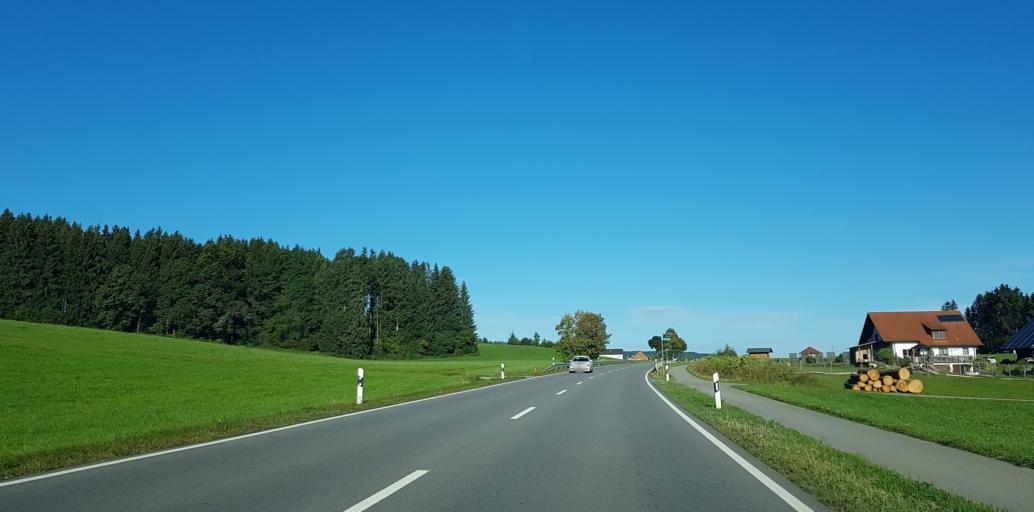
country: DE
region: Baden-Wuerttemberg
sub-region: Tuebingen Region
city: Bad Wurzach
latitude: 47.8500
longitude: 9.9335
